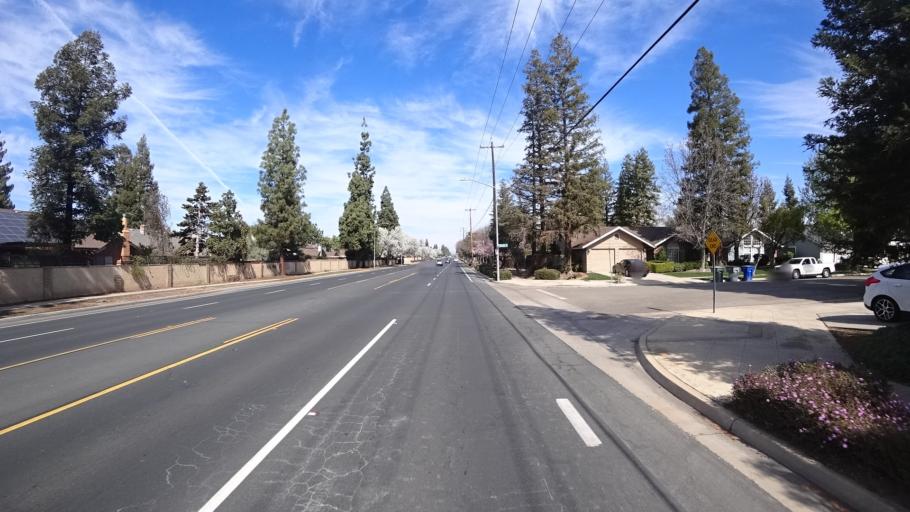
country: US
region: California
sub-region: Fresno County
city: Clovis
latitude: 36.8469
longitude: -119.7657
